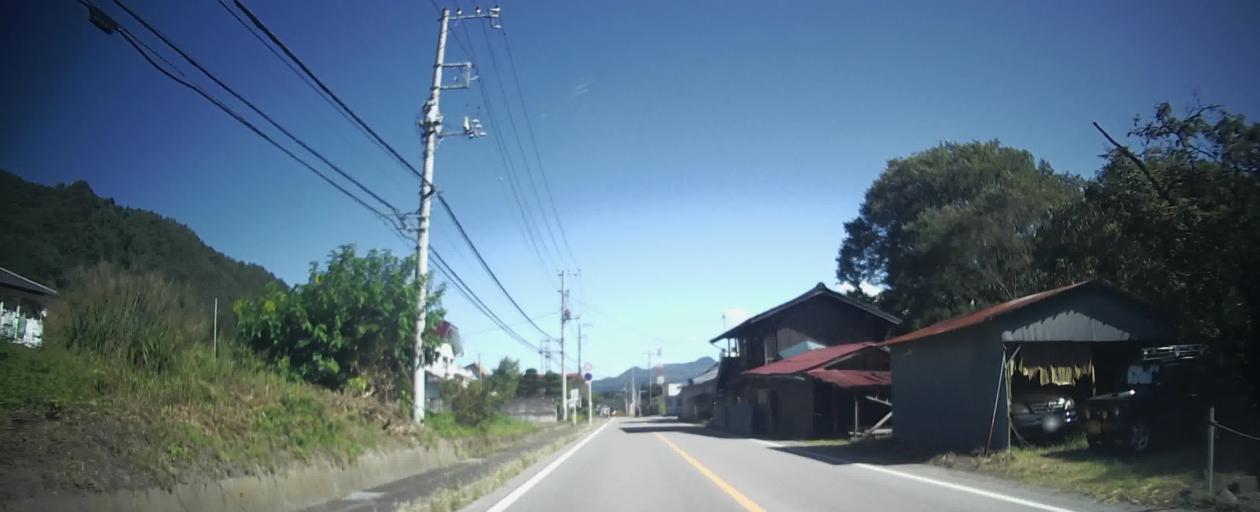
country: JP
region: Gunma
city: Nakanojomachi
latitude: 36.5702
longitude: 138.7425
